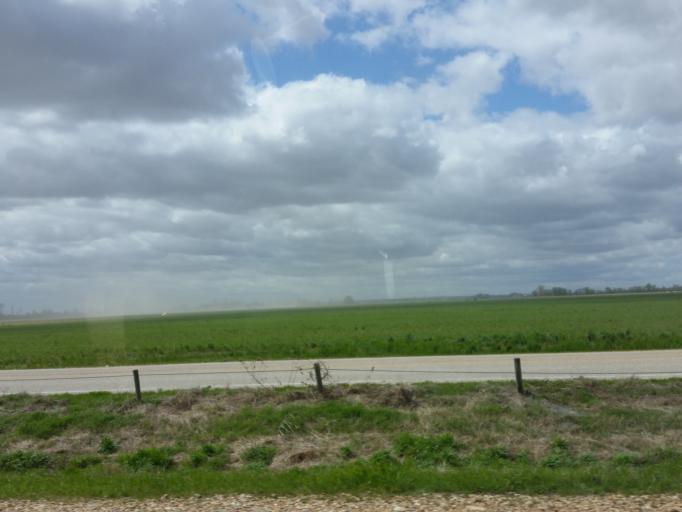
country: US
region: Arkansas
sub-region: Poinsett County
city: Trumann
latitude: 35.6294
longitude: -90.5020
